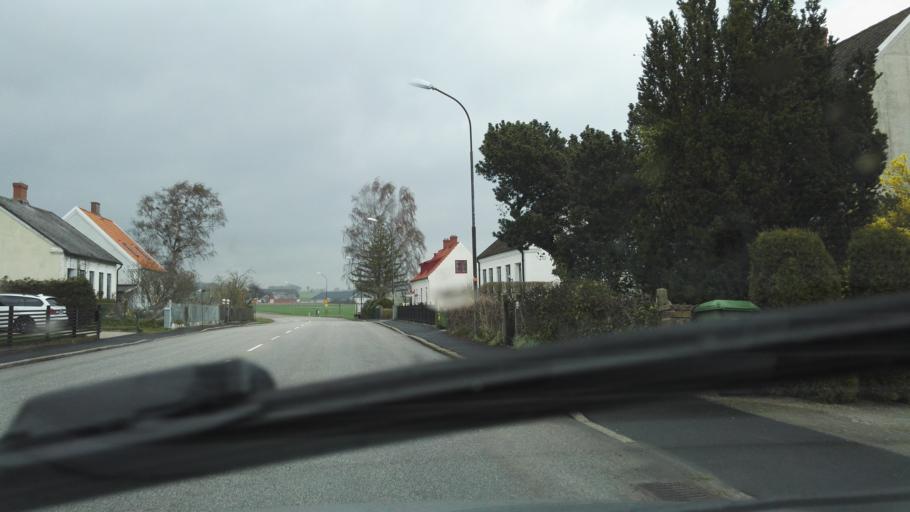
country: SE
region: Skane
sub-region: Simrishamns Kommun
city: Simrishamn
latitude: 55.4777
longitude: 14.2833
